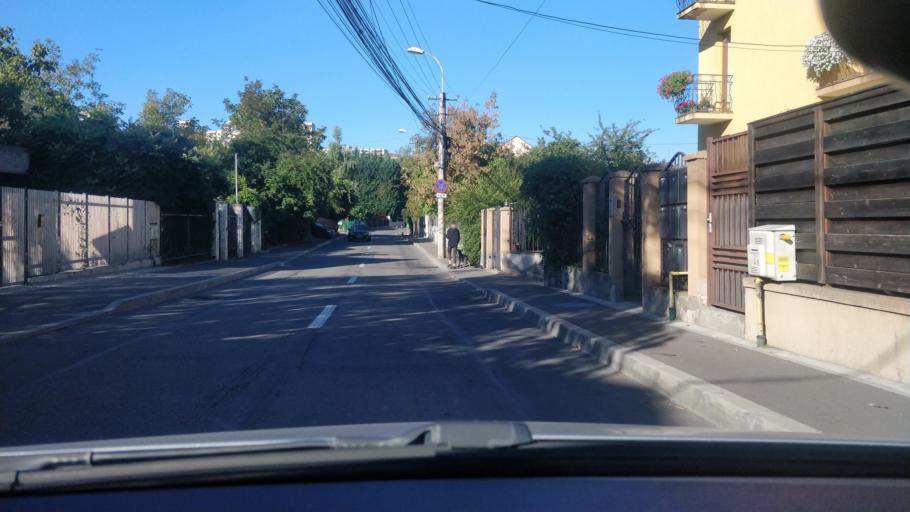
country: RO
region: Cluj
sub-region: Municipiul Cluj-Napoca
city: Cluj-Napoca
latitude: 46.7573
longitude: 23.5877
